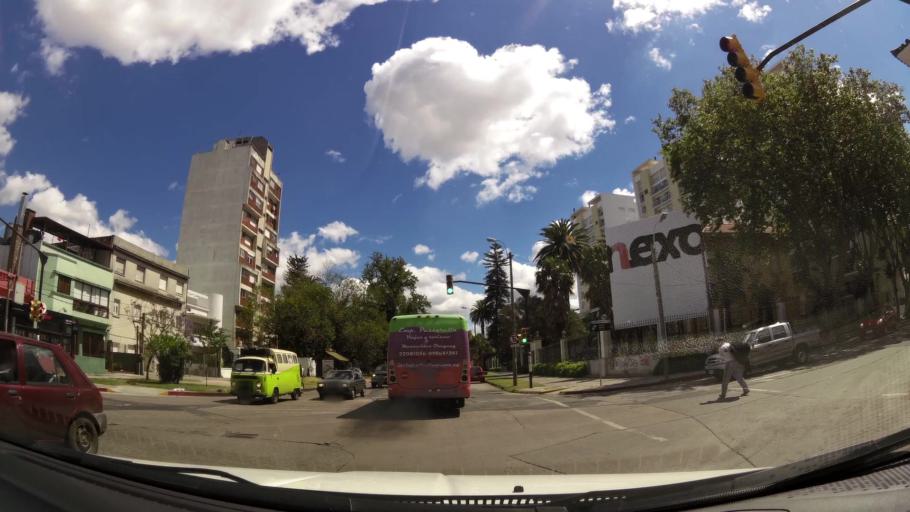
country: UY
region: Montevideo
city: Montevideo
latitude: -34.8749
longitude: -56.1966
